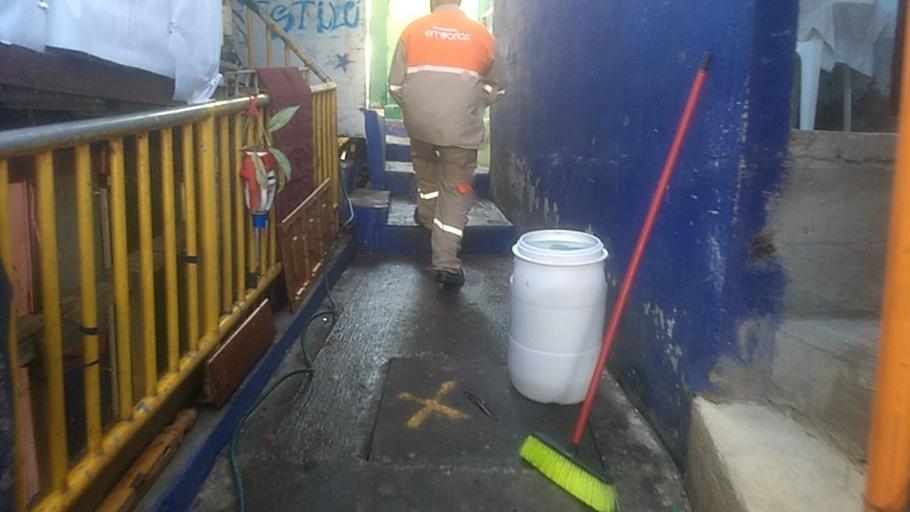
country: CO
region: Antioquia
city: Bello
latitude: 6.2968
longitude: -75.5498
